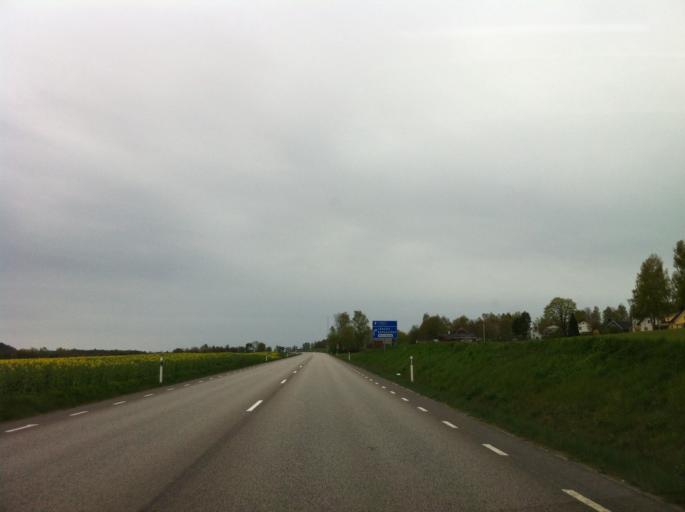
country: SE
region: Halland
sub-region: Falkenbergs Kommun
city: Falkenberg
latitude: 56.9846
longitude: 12.5806
